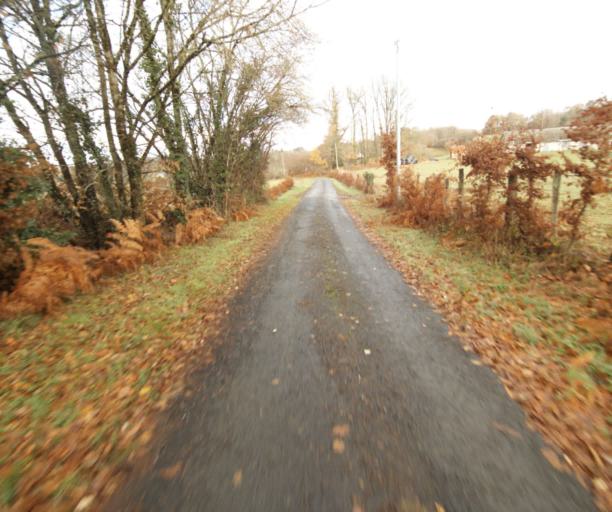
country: FR
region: Limousin
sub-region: Departement de la Correze
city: Saint-Mexant
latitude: 45.2493
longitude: 1.6479
